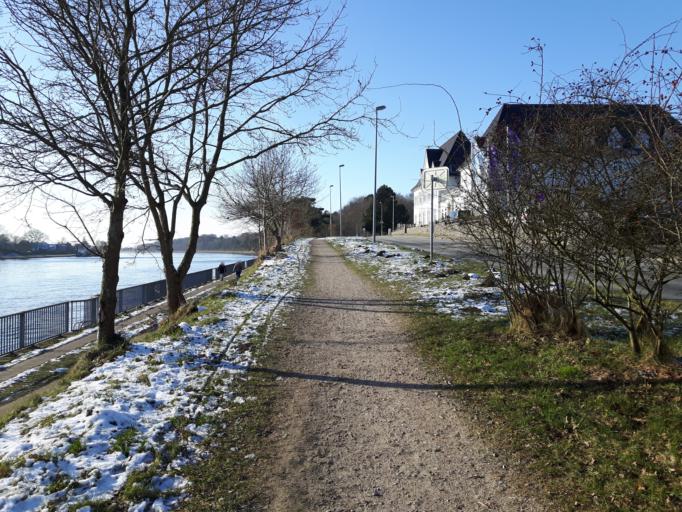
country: DE
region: Schleswig-Holstein
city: Westerronfeld
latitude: 54.2898
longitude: 9.6553
